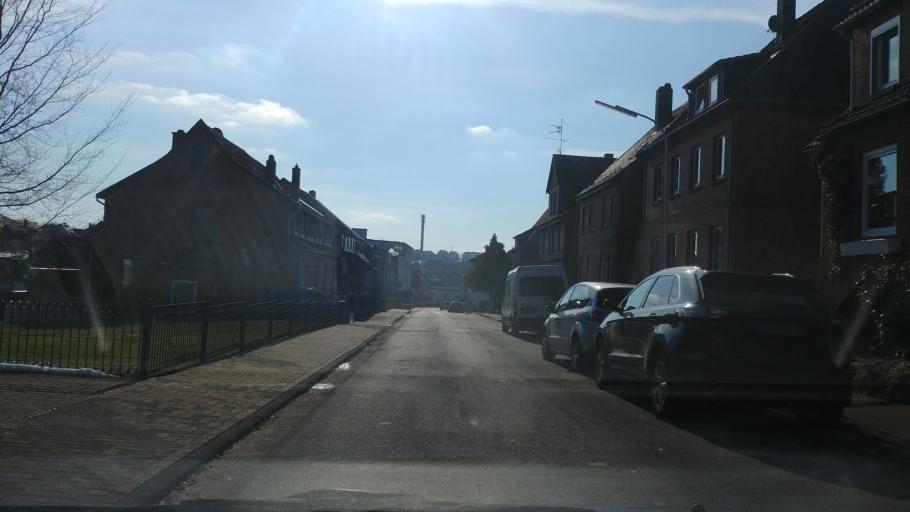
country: DE
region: Lower Saxony
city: Uslar
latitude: 51.6639
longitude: 9.6398
